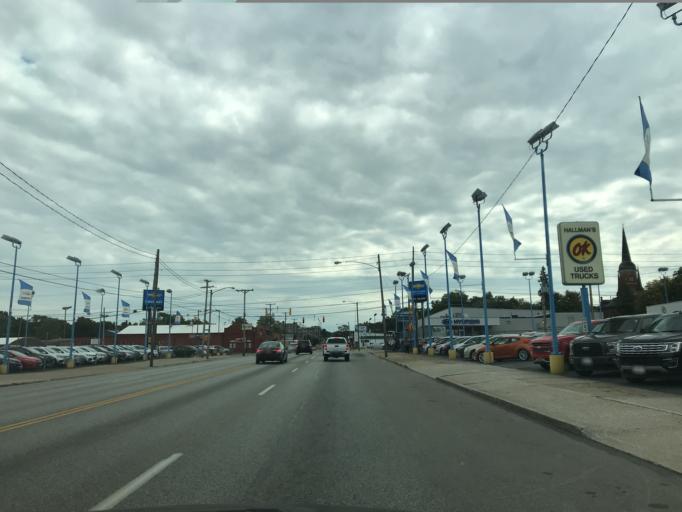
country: US
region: Pennsylvania
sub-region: Erie County
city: Erie
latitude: 42.1168
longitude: -80.0769
